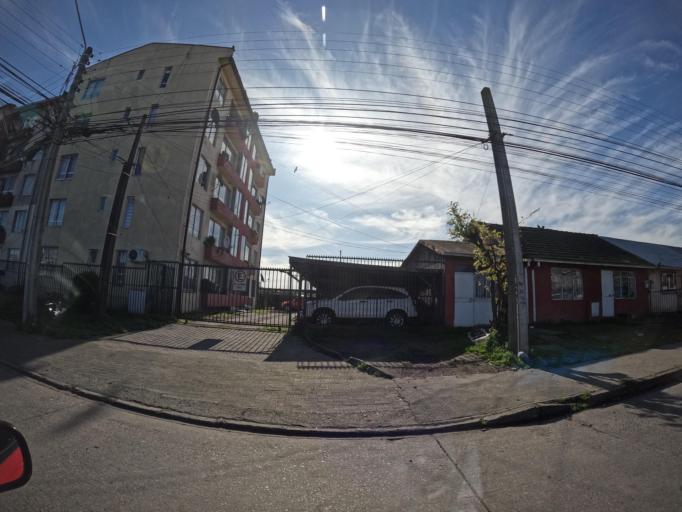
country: CL
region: Biobio
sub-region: Provincia de Concepcion
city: Concepcion
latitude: -36.8073
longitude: -73.0768
